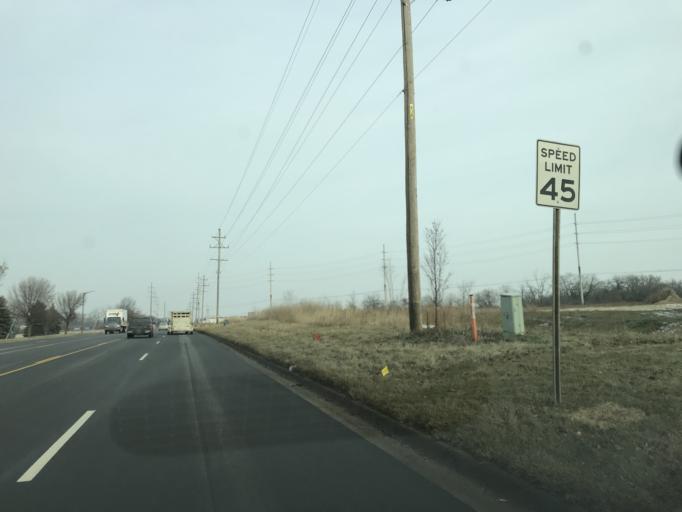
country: US
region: Michigan
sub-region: Ottawa County
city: Holland
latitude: 42.7555
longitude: -86.0770
